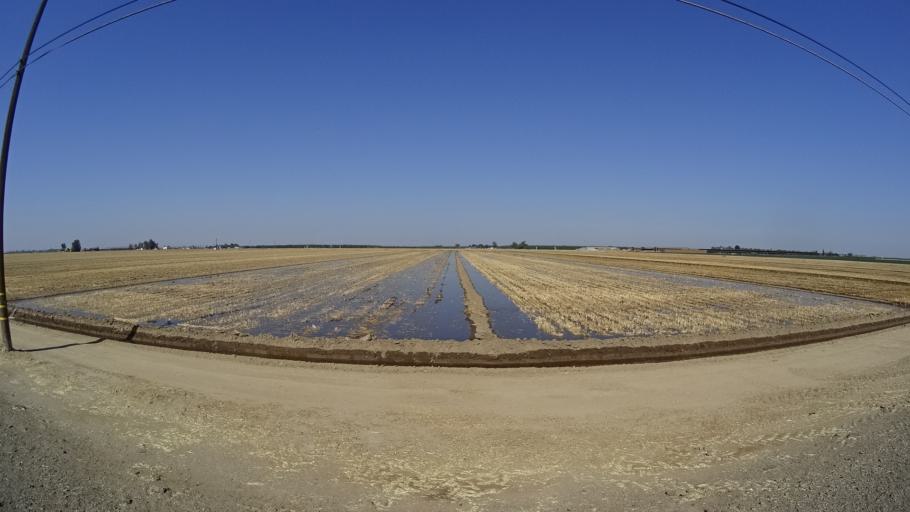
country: US
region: California
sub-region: Kings County
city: Hanford
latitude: 36.3633
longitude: -119.5650
